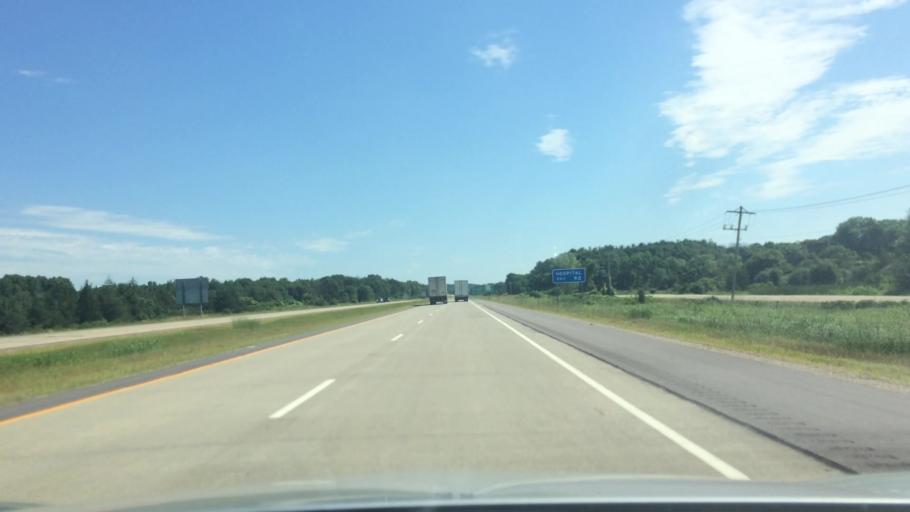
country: US
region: Wisconsin
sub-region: Columbia County
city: Portage
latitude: 43.5649
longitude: -89.4858
